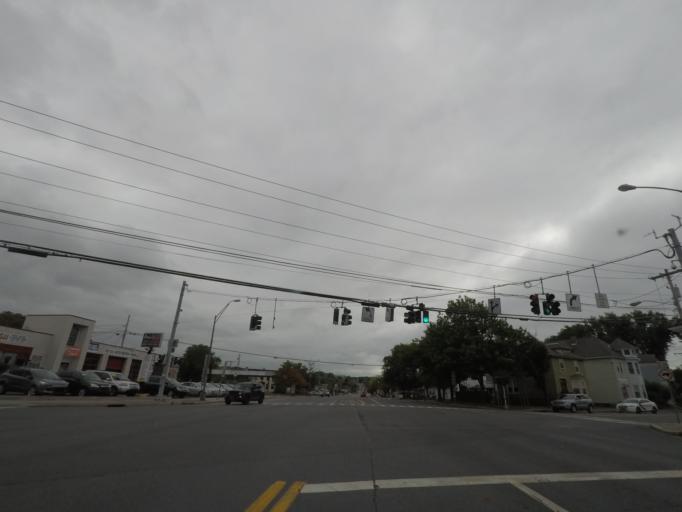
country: US
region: New York
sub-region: Rensselaer County
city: Rensselaer
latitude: 42.6377
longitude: -73.7483
